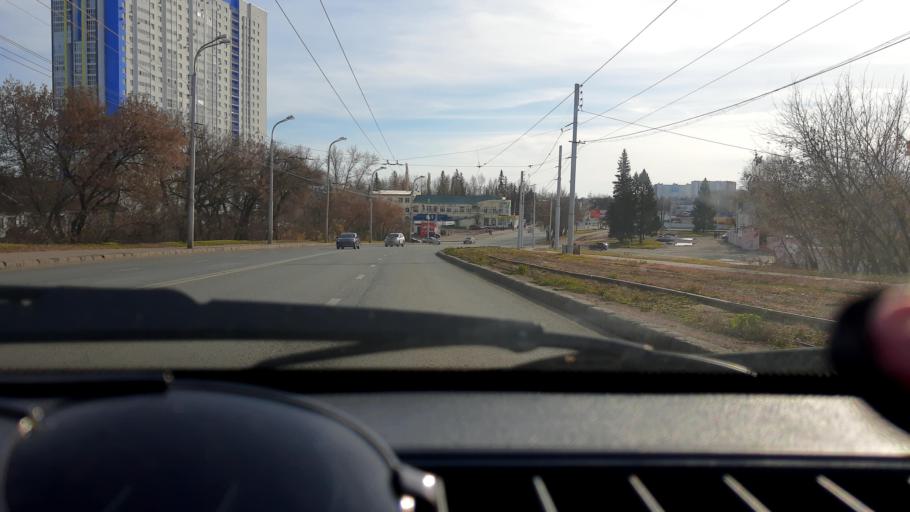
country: RU
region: Bashkortostan
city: Ufa
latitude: 54.8001
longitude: 56.1387
